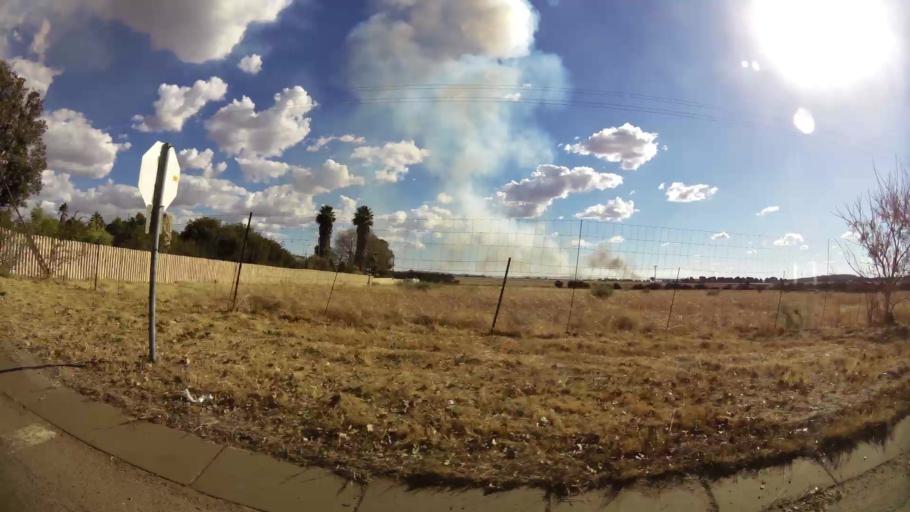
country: ZA
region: North-West
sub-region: Dr Kenneth Kaunda District Municipality
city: Klerksdorp
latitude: -26.8227
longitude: 26.6500
